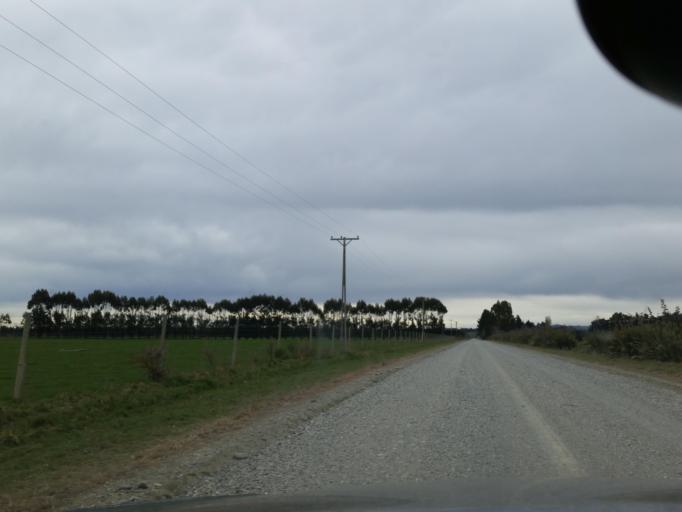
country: NZ
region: Southland
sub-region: Gore District
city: Gore
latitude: -45.8136
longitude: 168.7041
